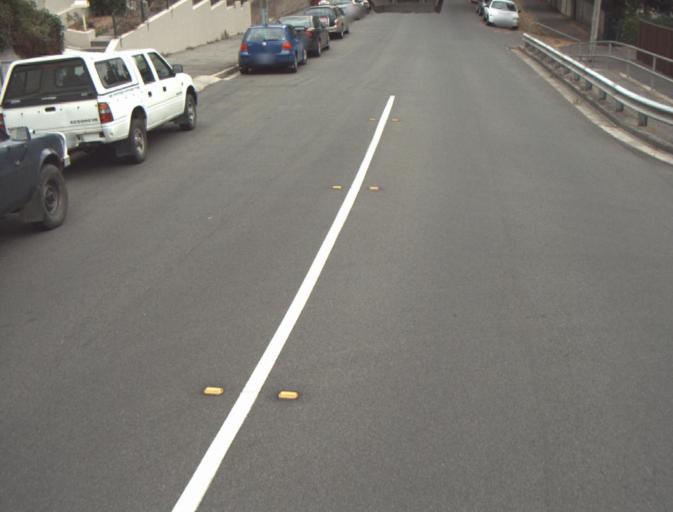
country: AU
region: Tasmania
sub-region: Launceston
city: East Launceston
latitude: -41.4402
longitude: 147.1454
